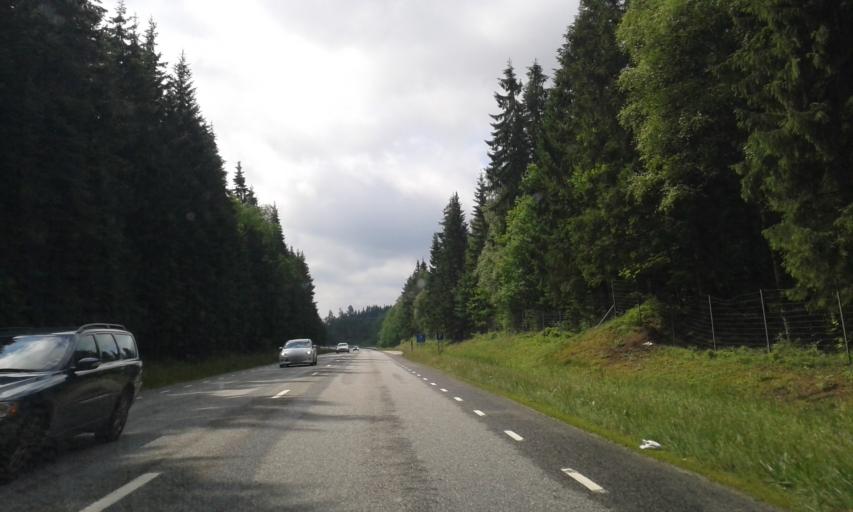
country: SE
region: Vaestra Goetaland
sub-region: Tranemo Kommun
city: Limmared
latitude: 57.5124
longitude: 13.3411
